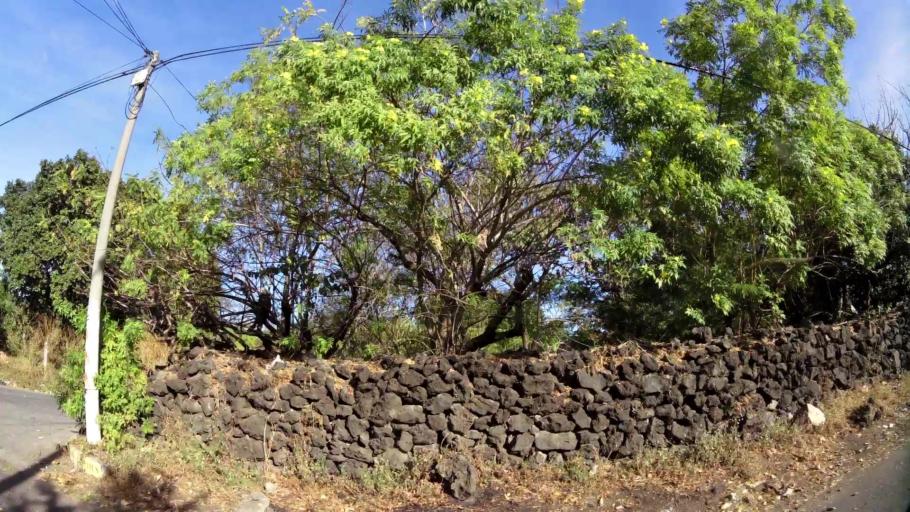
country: SV
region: San Miguel
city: San Miguel
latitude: 13.4694
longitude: -88.1867
